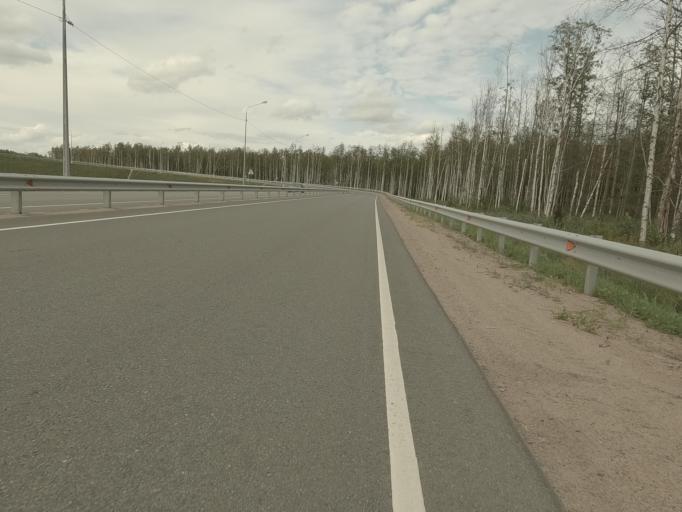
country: RU
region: Leningrad
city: Mga
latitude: 59.7564
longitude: 31.0946
